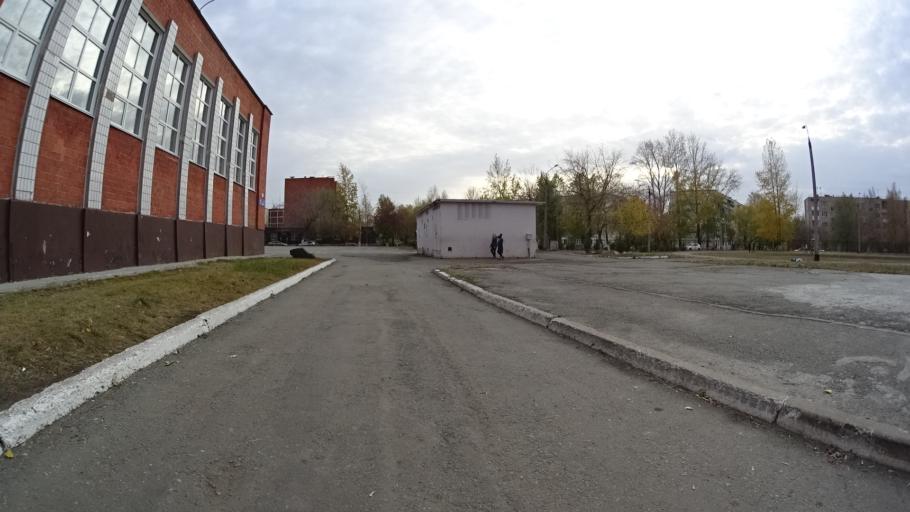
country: RU
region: Chelyabinsk
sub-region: Gorod Chelyabinsk
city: Chelyabinsk
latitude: 55.1919
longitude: 61.3089
